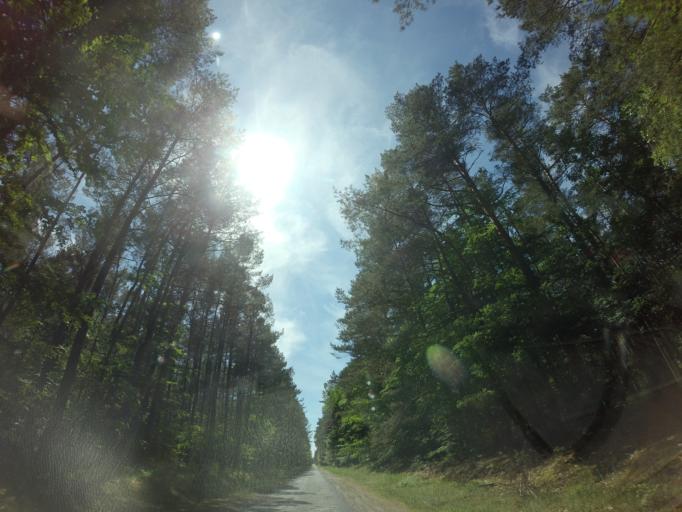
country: PL
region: West Pomeranian Voivodeship
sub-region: Powiat choszczenski
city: Drawno
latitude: 53.1419
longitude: 15.8629
